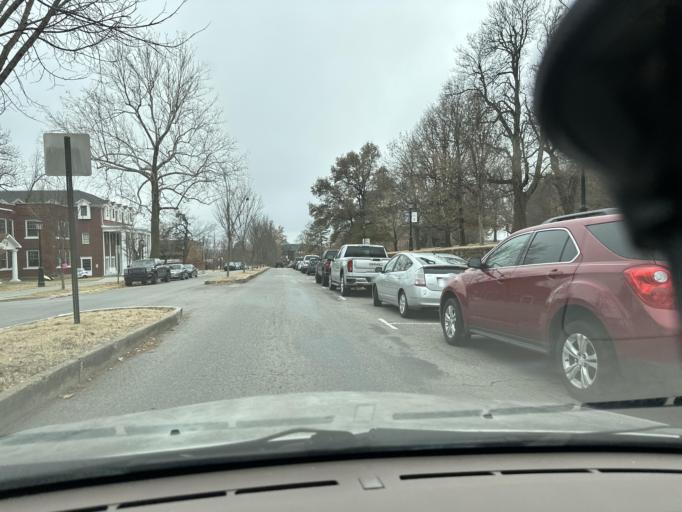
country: US
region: Arkansas
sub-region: Washington County
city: Fayetteville
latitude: 36.0686
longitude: -94.1685
